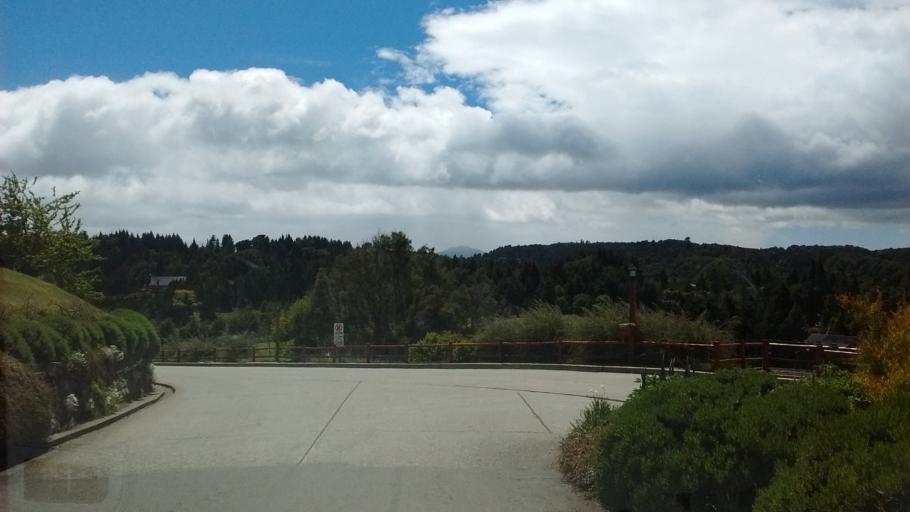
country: AR
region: Rio Negro
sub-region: Departamento de Bariloche
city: San Carlos de Bariloche
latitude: -41.0583
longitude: -71.5306
